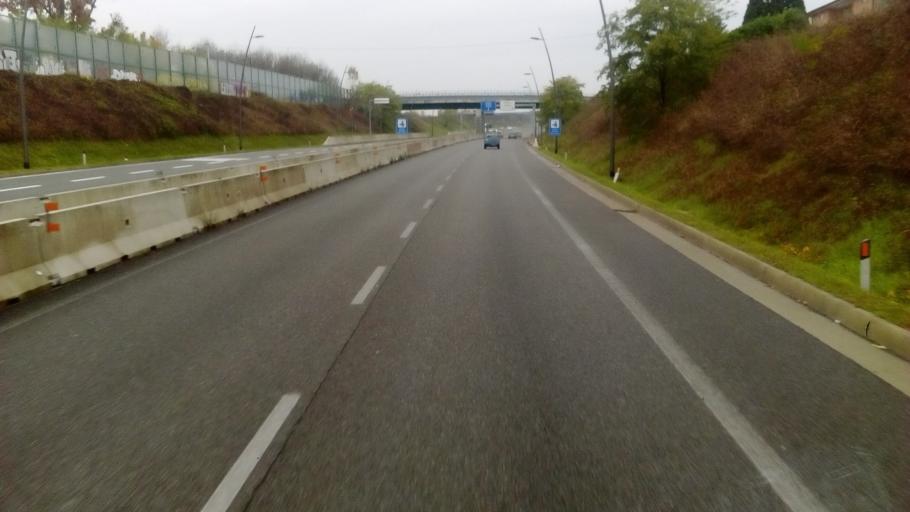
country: IT
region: Lombardy
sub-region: Provincia di Bergamo
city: Dalmine
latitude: 45.6574
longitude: 9.6135
